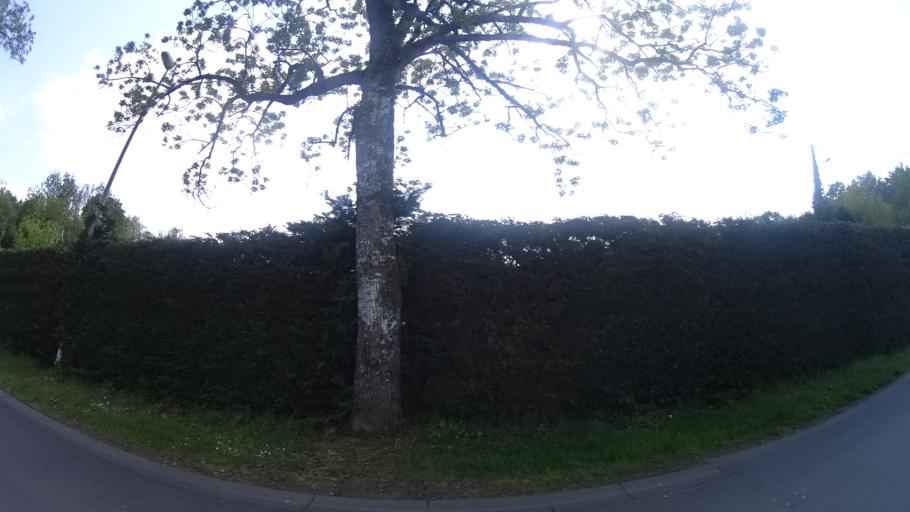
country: FR
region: Pays de la Loire
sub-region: Departement de la Loire-Atlantique
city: Saint-Nicolas-de-Redon
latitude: 47.6396
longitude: -2.0719
